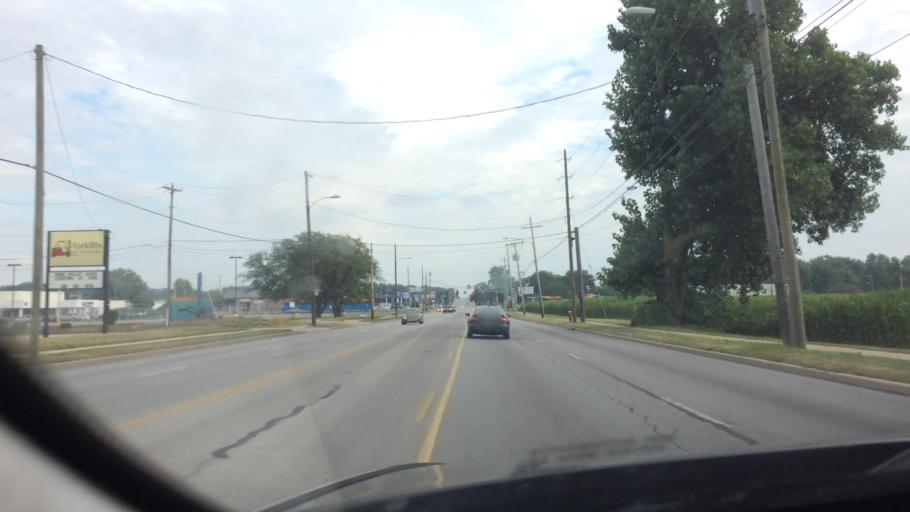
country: US
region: Ohio
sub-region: Lucas County
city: Ottawa Hills
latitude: 41.6410
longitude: -83.6260
